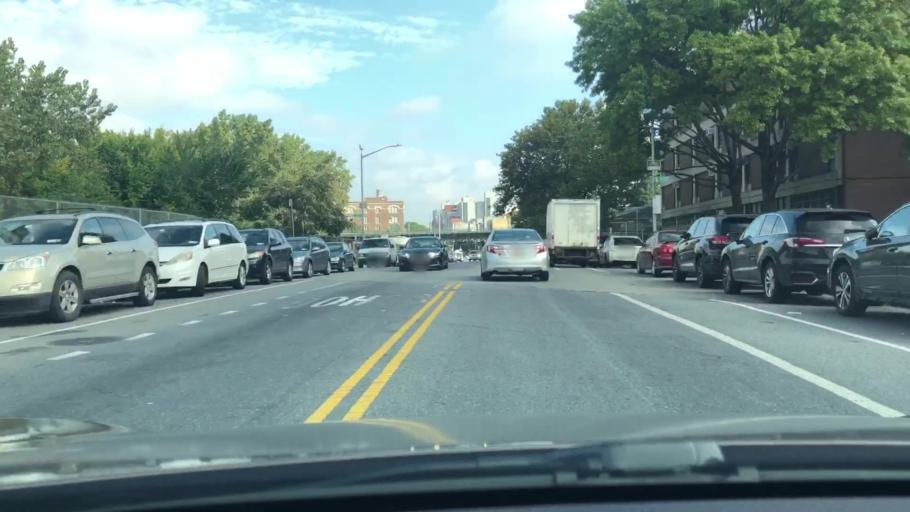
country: US
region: New York
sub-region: New York County
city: Inwood
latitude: 40.8145
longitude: -73.9128
